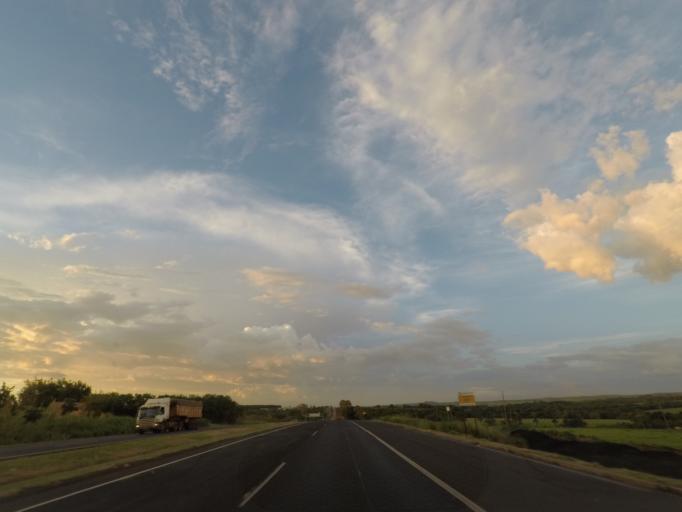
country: BR
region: Minas Gerais
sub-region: Uberaba
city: Uberaba
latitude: -19.6824
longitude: -47.9937
